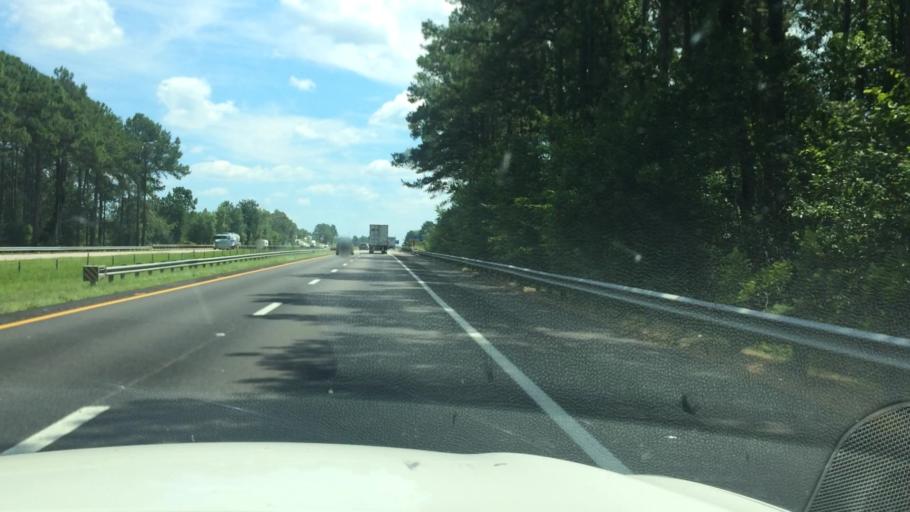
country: US
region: South Carolina
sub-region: Aiken County
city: Aiken
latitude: 33.6492
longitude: -81.7156
